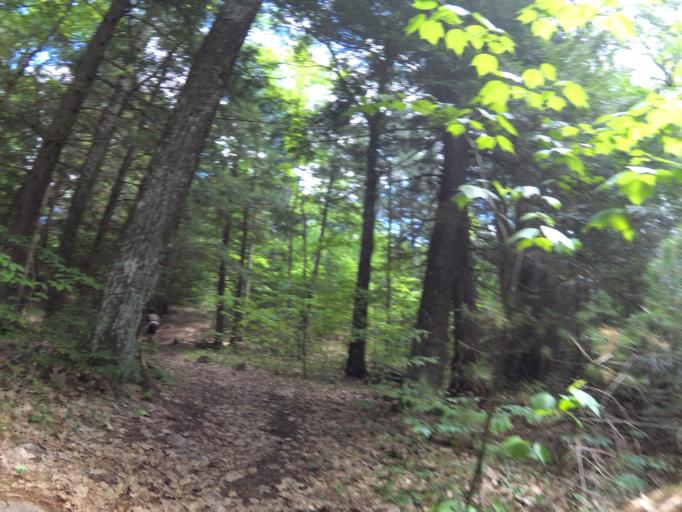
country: CA
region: Ontario
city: Renfrew
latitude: 45.0561
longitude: -76.8484
